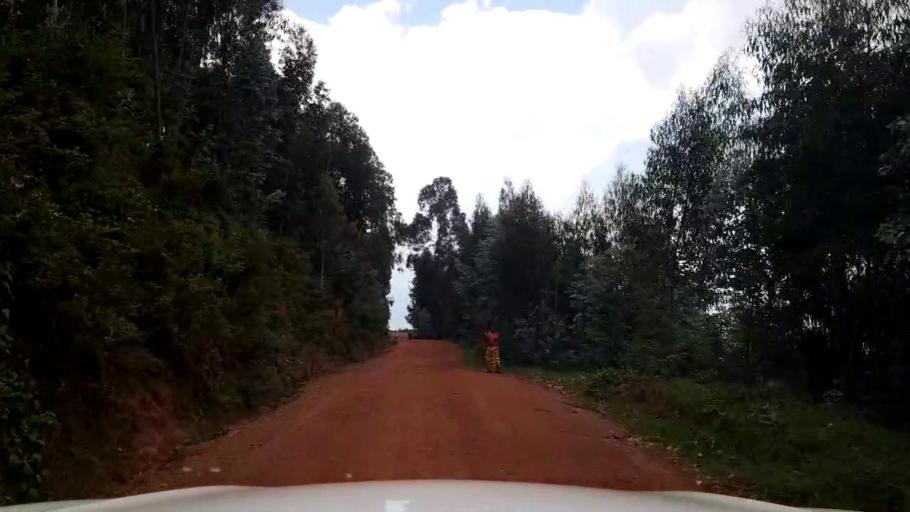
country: RW
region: Northern Province
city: Byumba
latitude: -1.5266
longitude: 29.9622
